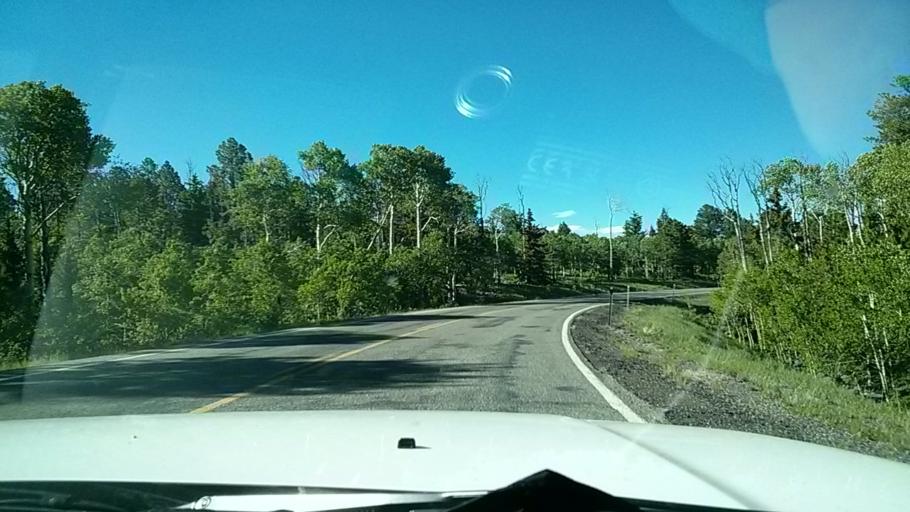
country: US
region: Utah
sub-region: Wayne County
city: Loa
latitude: 38.0788
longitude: -111.3395
